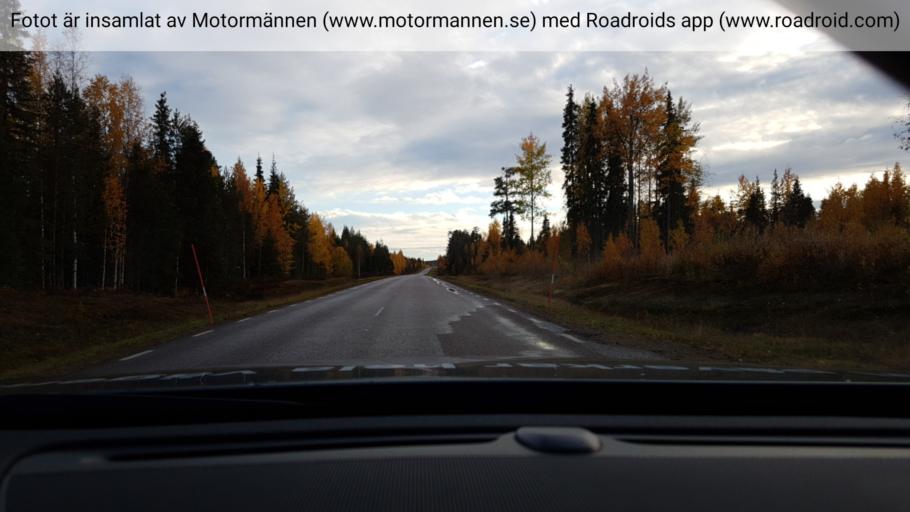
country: SE
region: Norrbotten
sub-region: Overkalix Kommun
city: OEverkalix
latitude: 66.8895
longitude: 22.7692
